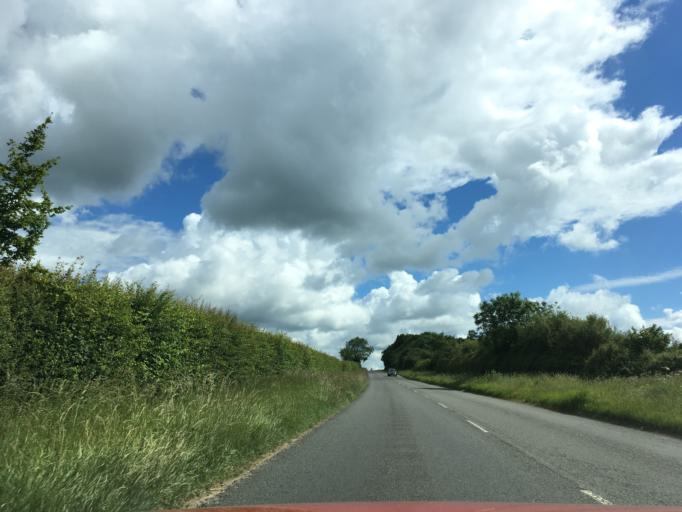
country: GB
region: England
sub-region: Oxfordshire
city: Burford
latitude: 51.8209
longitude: -1.6178
